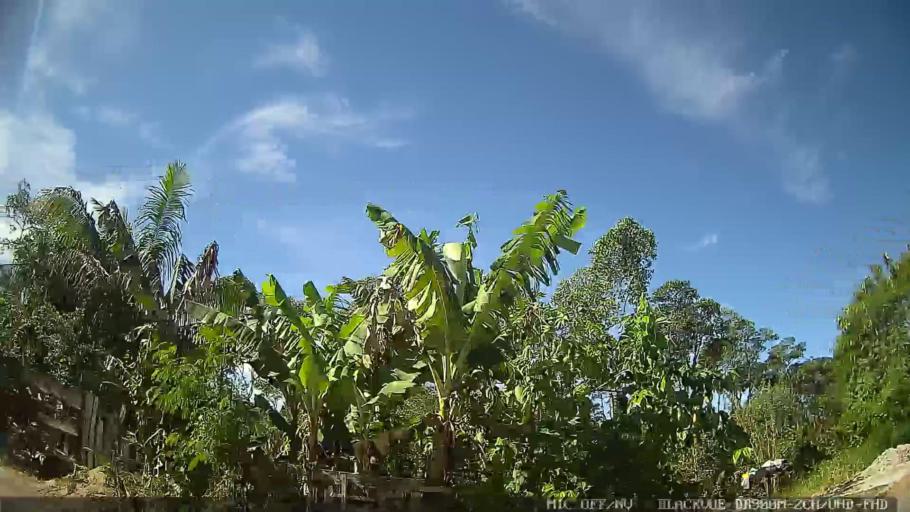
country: BR
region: Sao Paulo
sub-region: Santos
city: Santos
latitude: -23.9326
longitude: -46.2867
